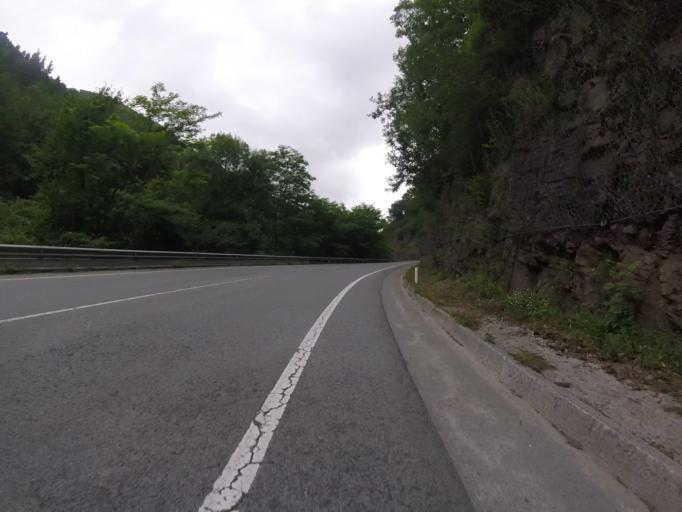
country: ES
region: Navarre
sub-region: Provincia de Navarra
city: Saldias
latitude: 43.1074
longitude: -1.7669
